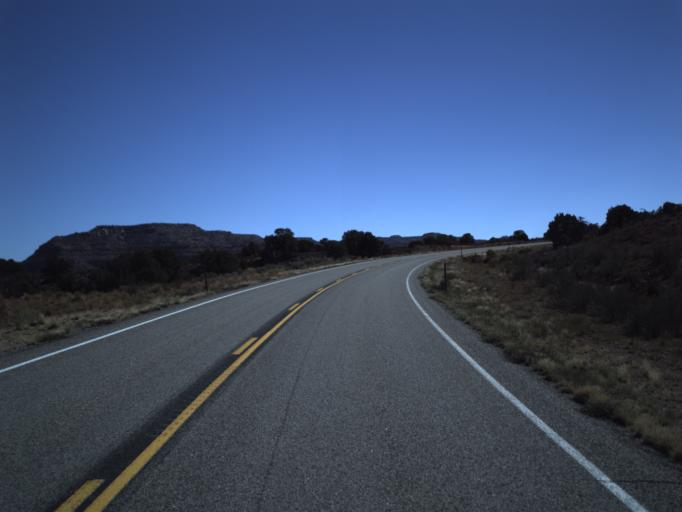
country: US
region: Utah
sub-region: San Juan County
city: Blanding
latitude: 37.6565
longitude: -110.1764
